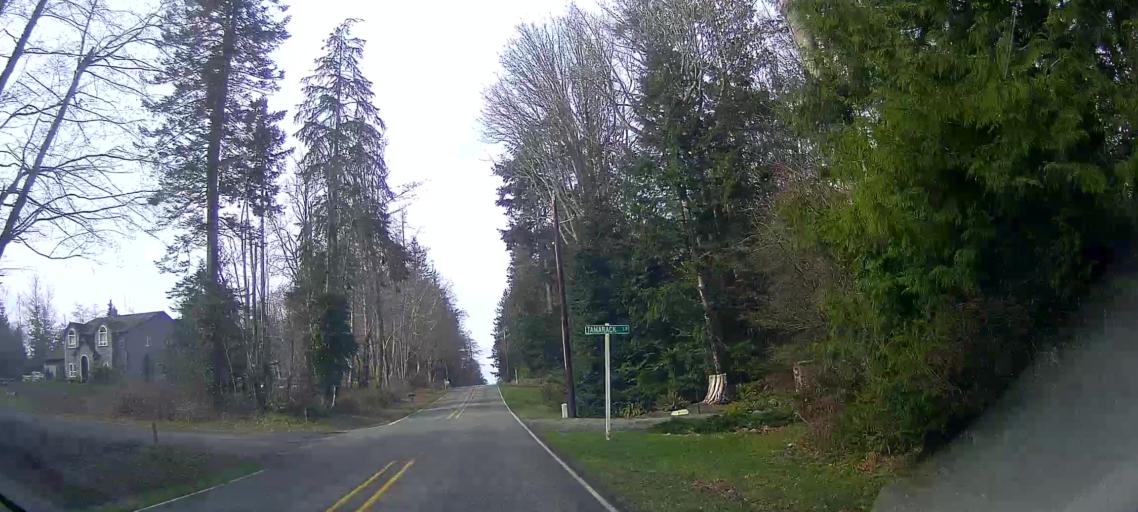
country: US
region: Washington
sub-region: Island County
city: Langley
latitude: 48.0854
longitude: -122.3823
